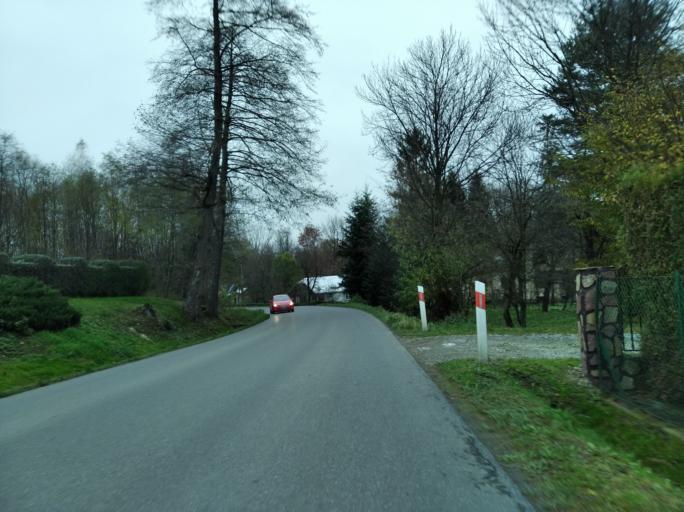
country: PL
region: Subcarpathian Voivodeship
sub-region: Powiat krosnienski
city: Chorkowka
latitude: 49.6749
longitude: 21.6819
